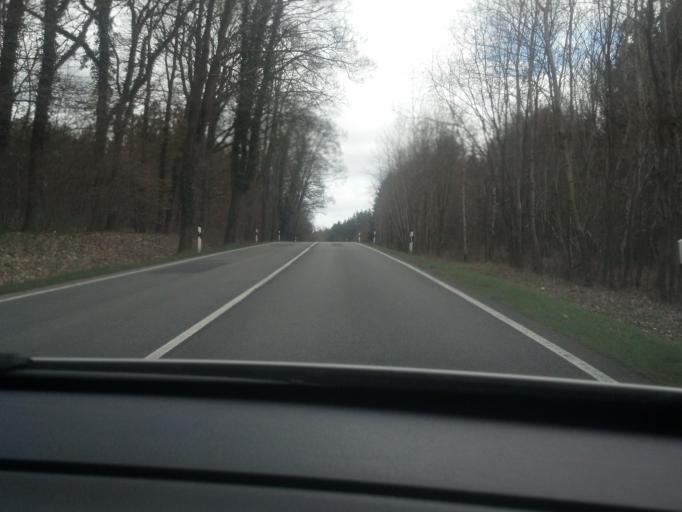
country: DE
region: Mecklenburg-Vorpommern
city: Malchow
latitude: 53.3644
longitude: 12.3919
